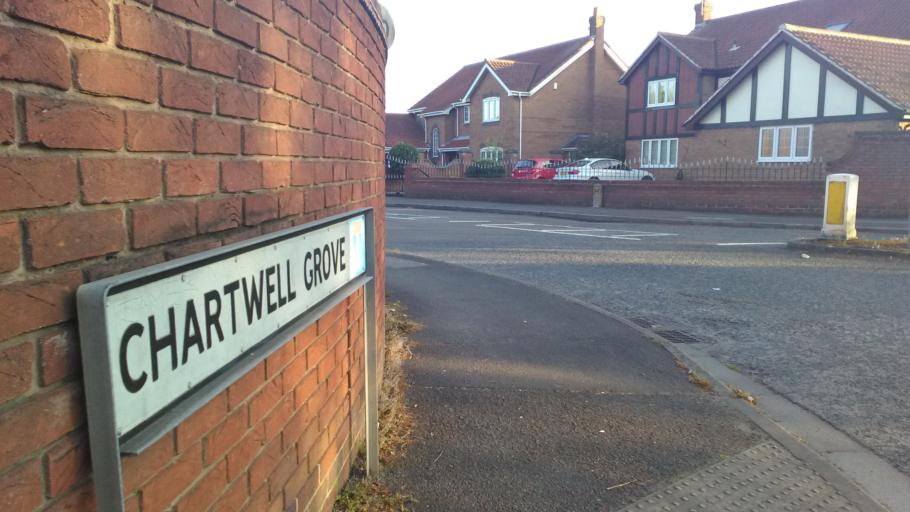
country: GB
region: England
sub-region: Nottinghamshire
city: Arnold
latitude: 52.9937
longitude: -1.1053
